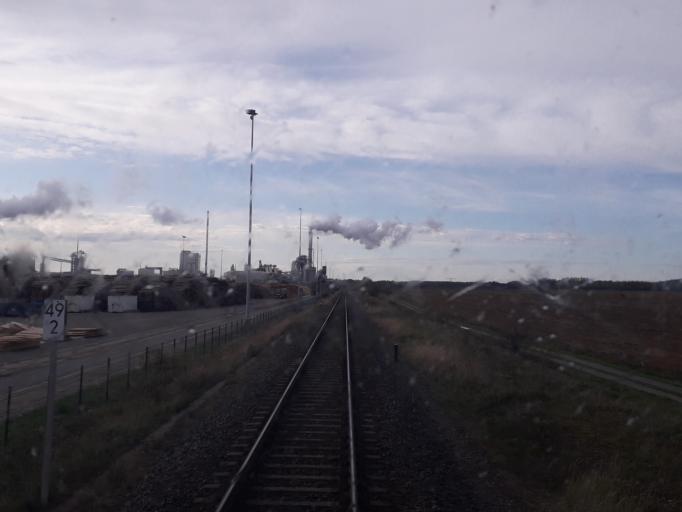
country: DE
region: Brandenburg
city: Heiligengrabe
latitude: 53.1514
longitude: 12.3883
